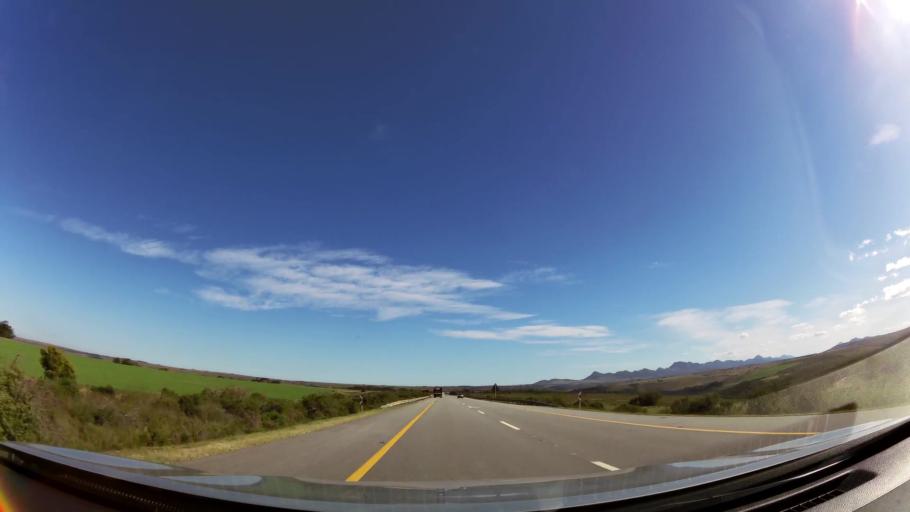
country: ZA
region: Eastern Cape
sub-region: Cacadu District Municipality
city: Kruisfontein
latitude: -34.0226
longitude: 24.6133
